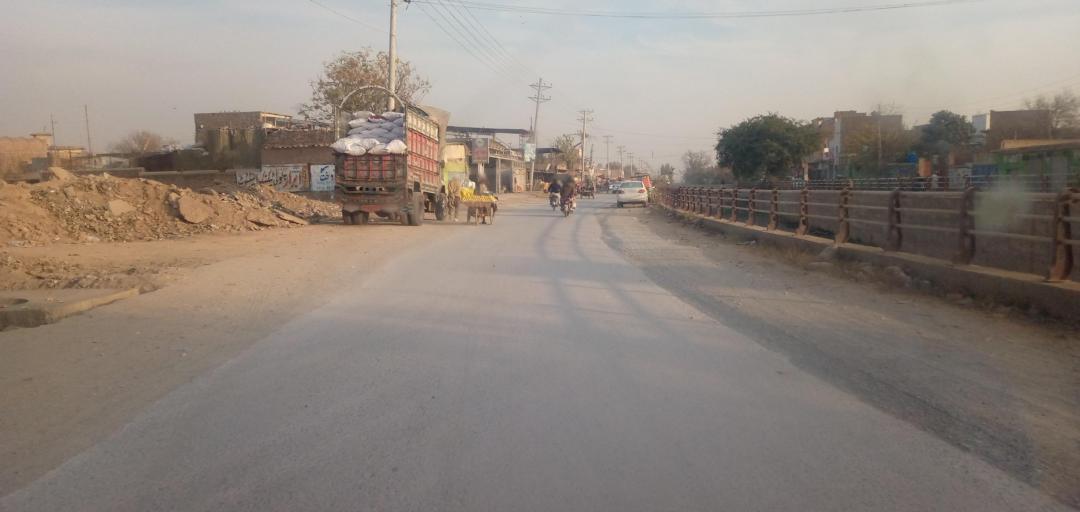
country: PK
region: Khyber Pakhtunkhwa
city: Peshawar
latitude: 33.9738
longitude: 71.5290
